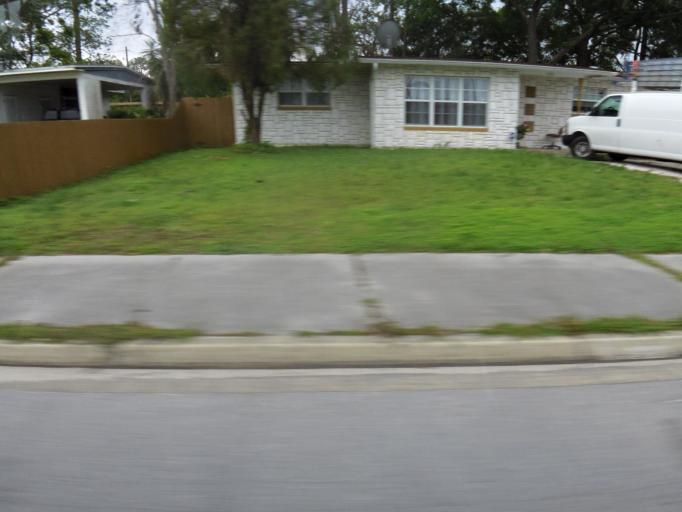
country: US
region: Florida
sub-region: Duval County
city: Jacksonville
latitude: 30.2766
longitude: -81.6157
